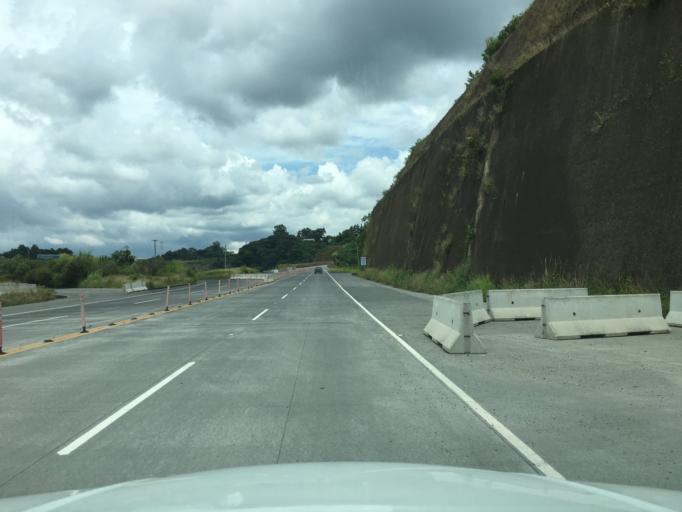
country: GT
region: Guatemala
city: Petapa
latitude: 14.5006
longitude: -90.5445
